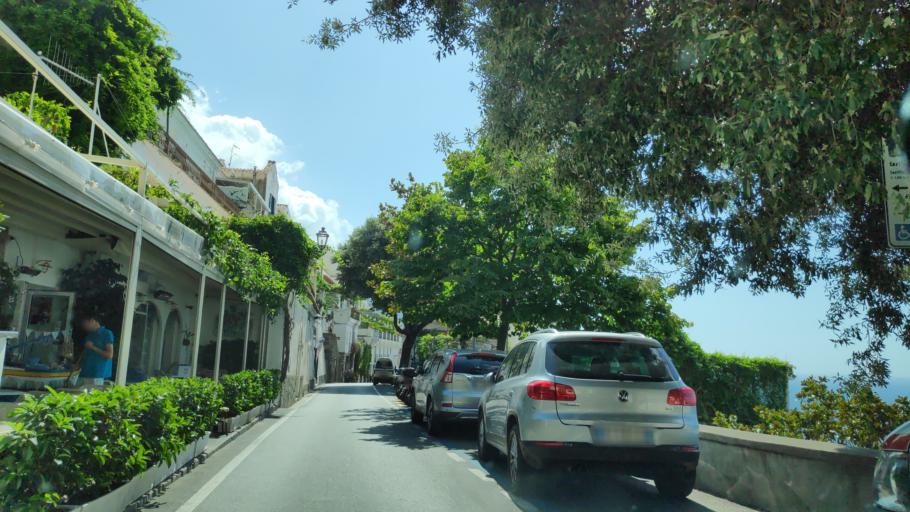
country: IT
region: Campania
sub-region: Provincia di Salerno
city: Positano
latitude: 40.6282
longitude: 14.4820
